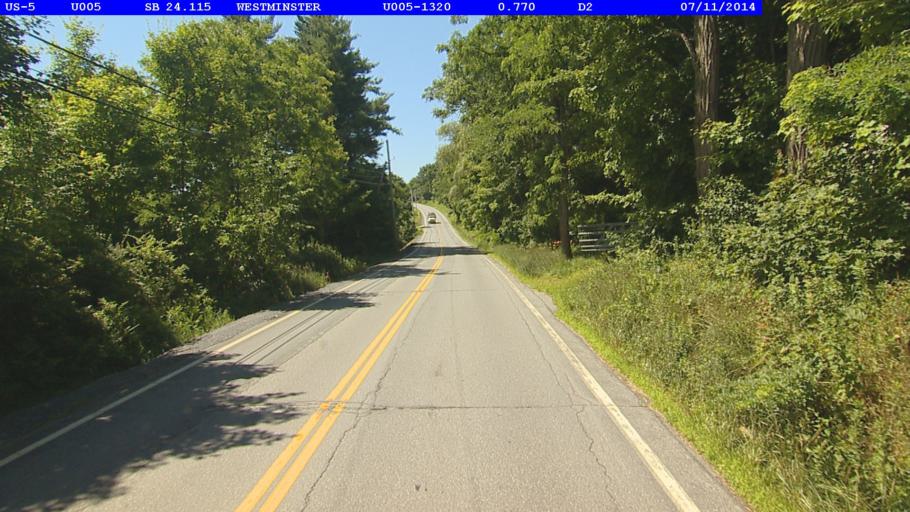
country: US
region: New Hampshire
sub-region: Cheshire County
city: Westmoreland
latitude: 43.0313
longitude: -72.4673
